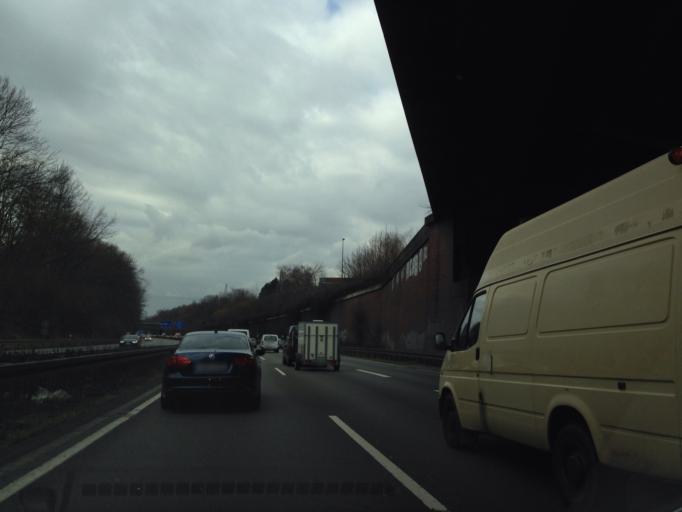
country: DE
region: North Rhine-Westphalia
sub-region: Regierungsbezirk Arnsberg
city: Herne
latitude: 51.5370
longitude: 7.2065
